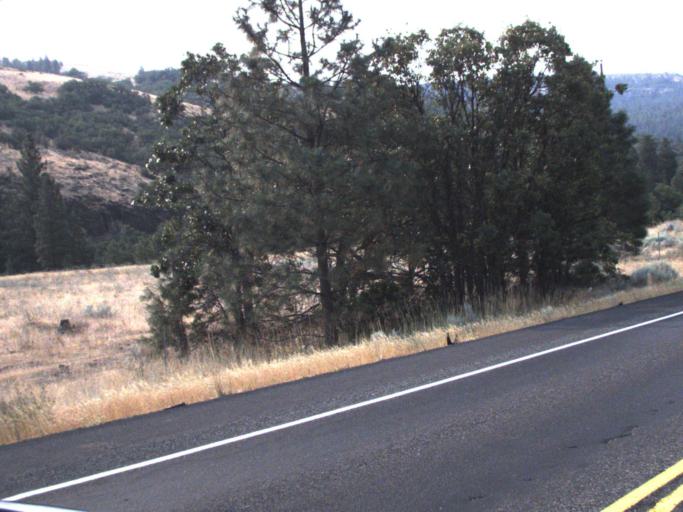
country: US
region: Washington
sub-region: Klickitat County
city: Goldendale
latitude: 46.0571
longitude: -120.5663
